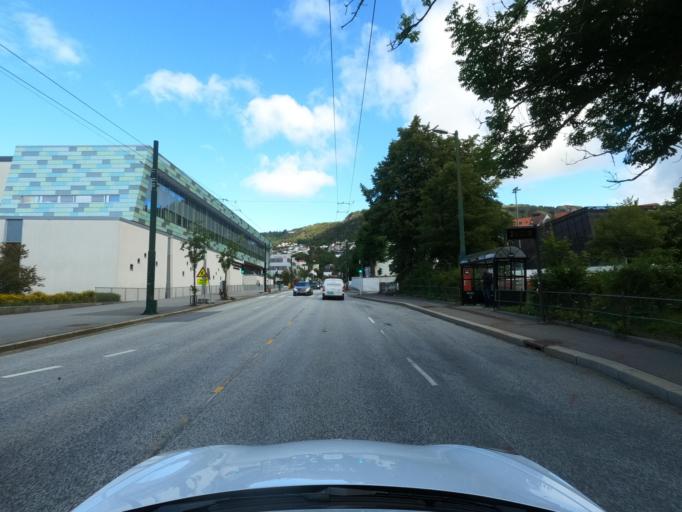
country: NO
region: Hordaland
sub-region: Bergen
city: Bergen
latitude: 60.3802
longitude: 5.3601
